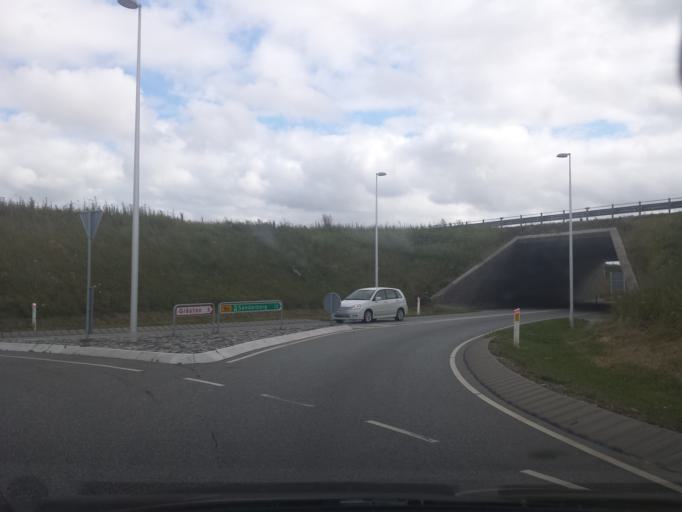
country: DK
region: South Denmark
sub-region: Sonderborg Kommune
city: Grasten
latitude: 54.9525
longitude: 9.6376
